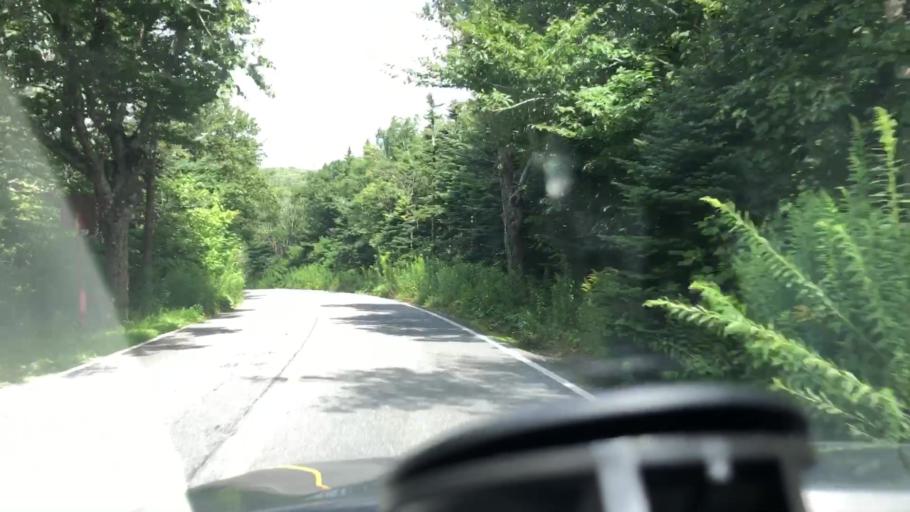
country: US
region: Massachusetts
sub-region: Berkshire County
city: Adams
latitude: 42.6430
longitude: -73.1632
